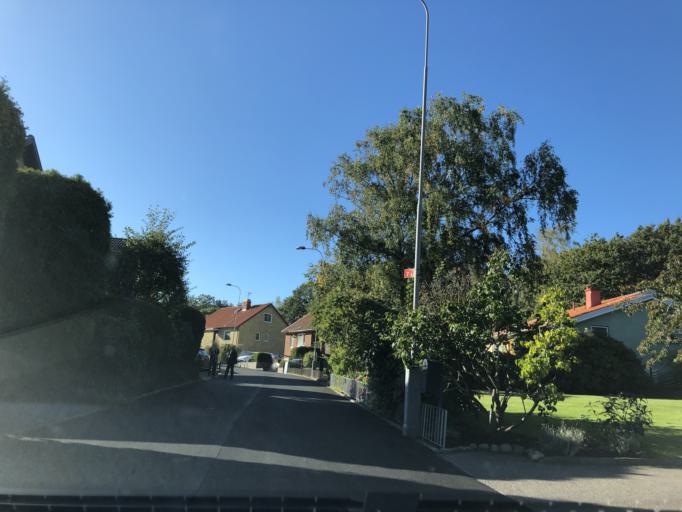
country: SE
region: Vaestra Goetaland
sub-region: Goteborg
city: Majorna
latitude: 57.6595
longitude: 11.8613
